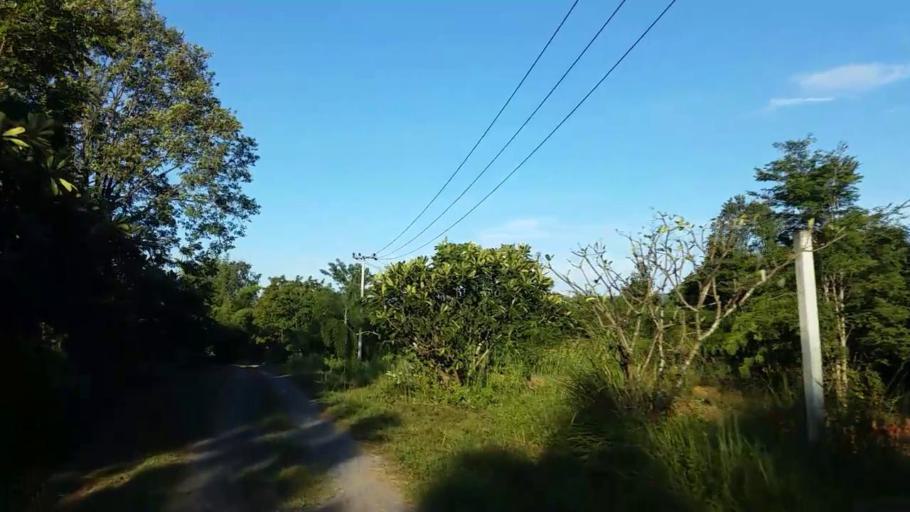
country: TH
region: Chaiyaphum
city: Thep Sathit
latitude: 15.5489
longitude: 101.4790
